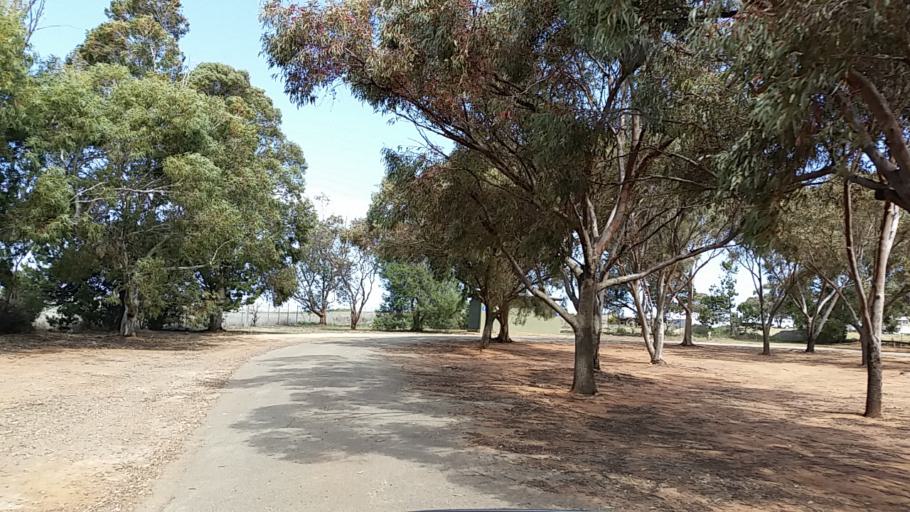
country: AU
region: South Australia
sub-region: Peterborough
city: Peterborough
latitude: -32.9802
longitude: 138.8351
